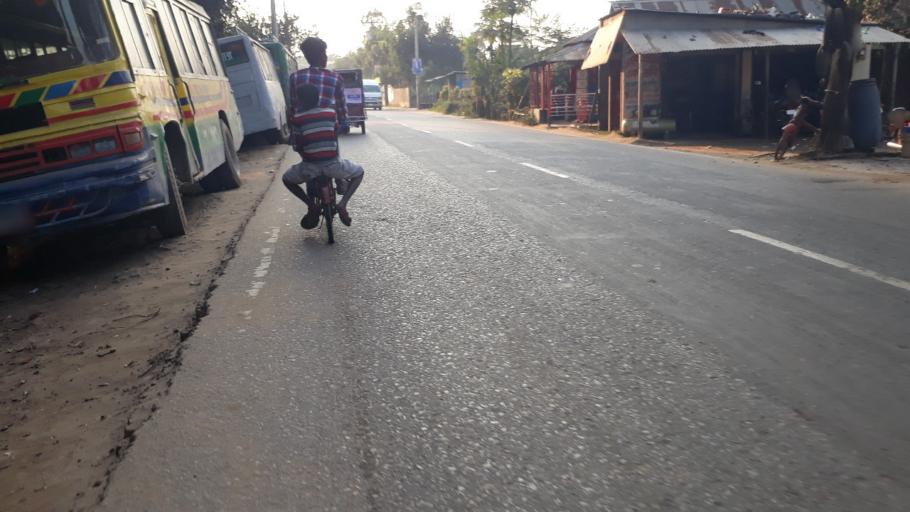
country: BD
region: Dhaka
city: Tungi
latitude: 23.8847
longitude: 90.3067
